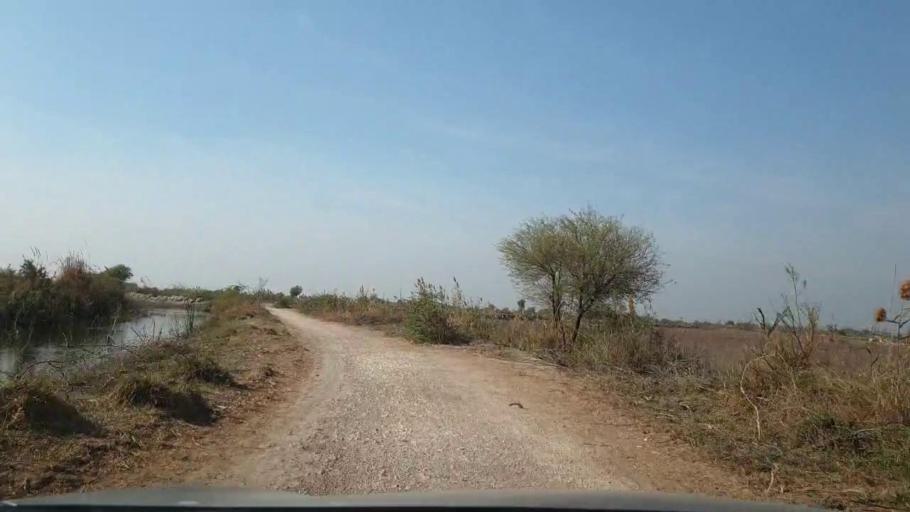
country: PK
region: Sindh
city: Berani
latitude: 25.7189
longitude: 68.7696
